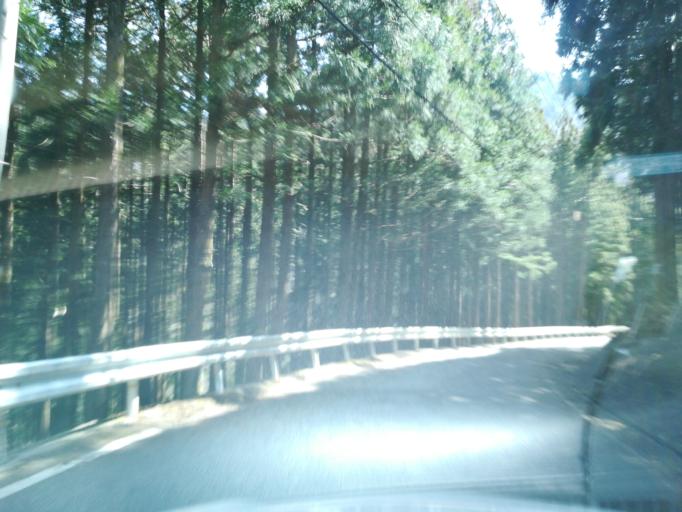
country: JP
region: Tokushima
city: Wakimachi
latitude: 33.8632
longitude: 134.0683
